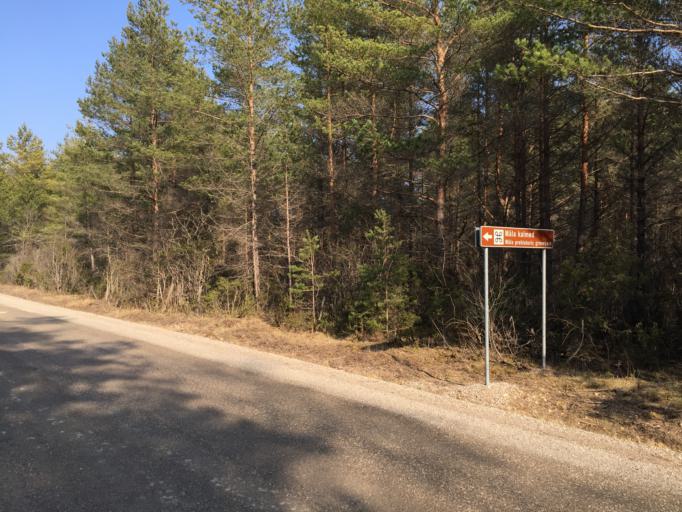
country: EE
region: Saare
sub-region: Orissaare vald
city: Orissaare
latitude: 58.5747
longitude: 23.2734
